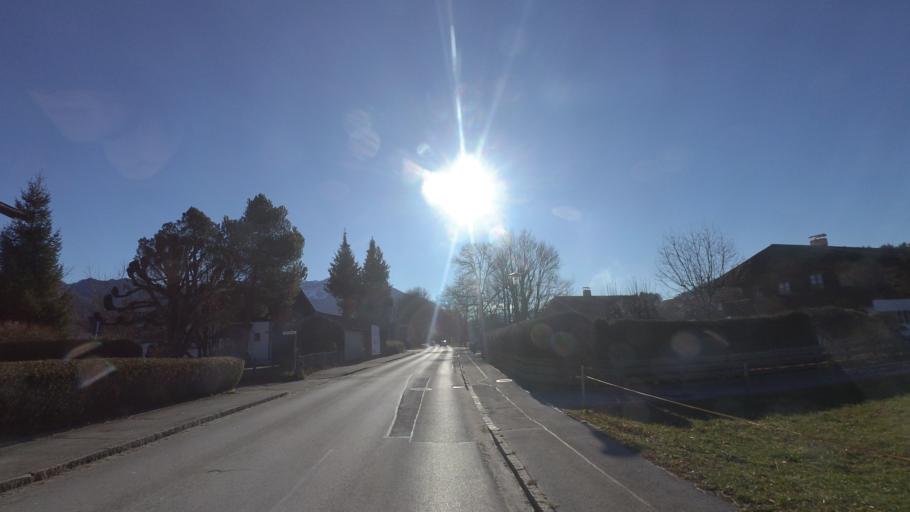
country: DE
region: Bavaria
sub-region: Upper Bavaria
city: Ubersee
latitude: 47.8127
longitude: 12.4804
